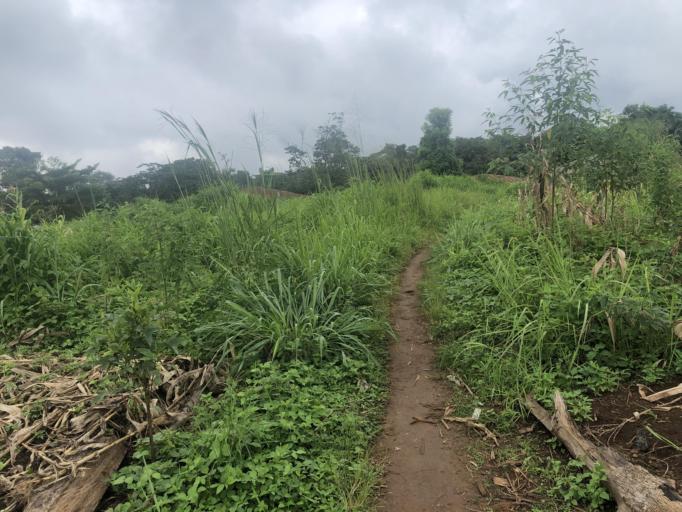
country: SL
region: Eastern Province
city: Kailahun
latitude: 8.2652
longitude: -10.5639
